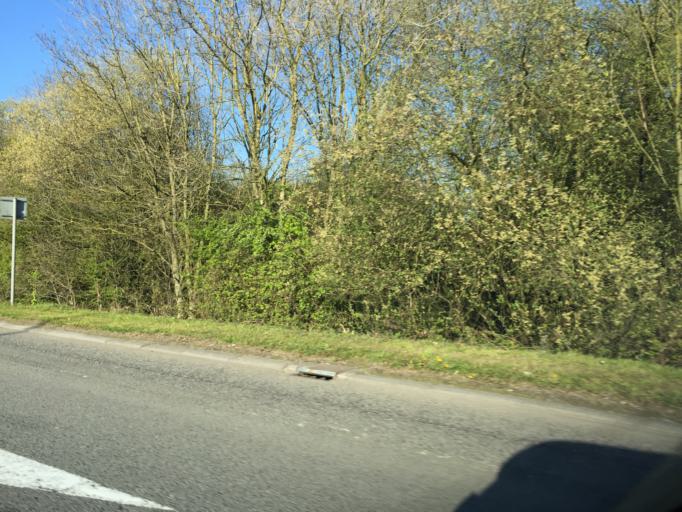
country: GB
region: Wales
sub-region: Cardiff
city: Cardiff
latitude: 51.5115
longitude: -3.1444
